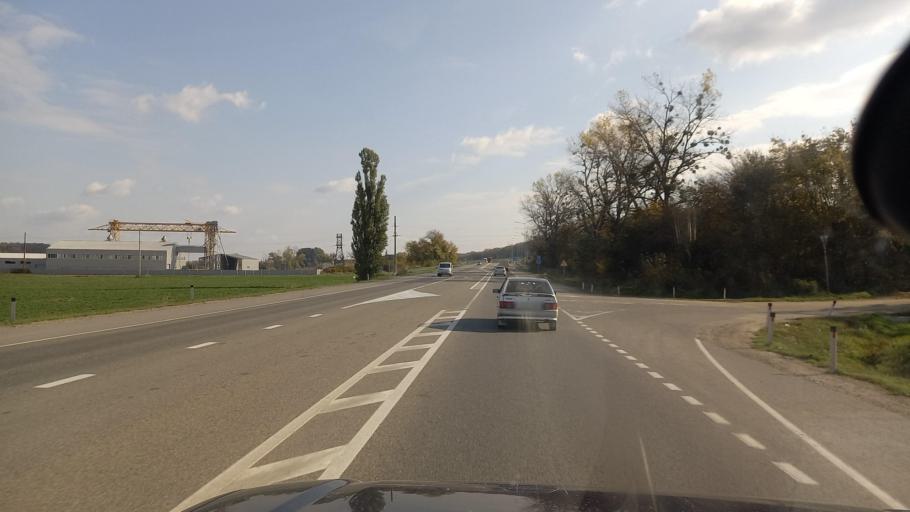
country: RU
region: Krasnodarskiy
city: Krymsk
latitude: 44.8731
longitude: 37.9129
